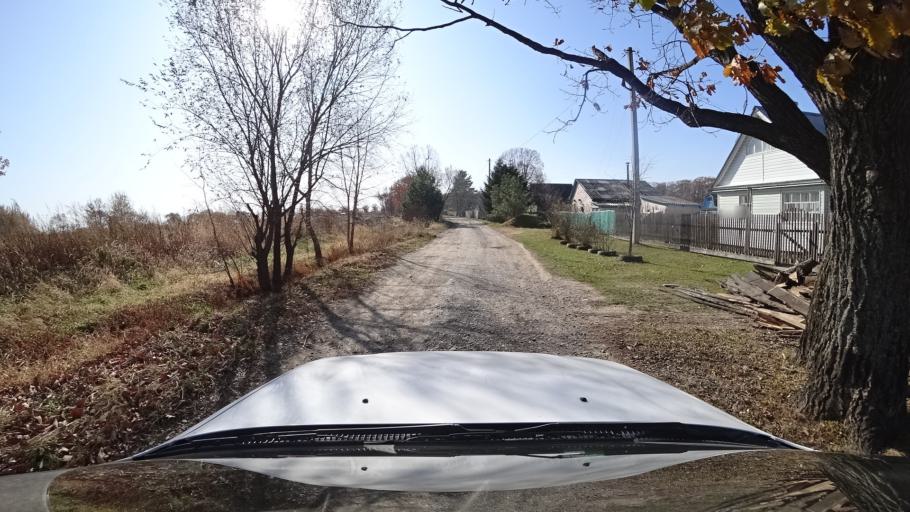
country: RU
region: Primorskiy
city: Dal'nerechensk
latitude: 45.8855
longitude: 133.7427
